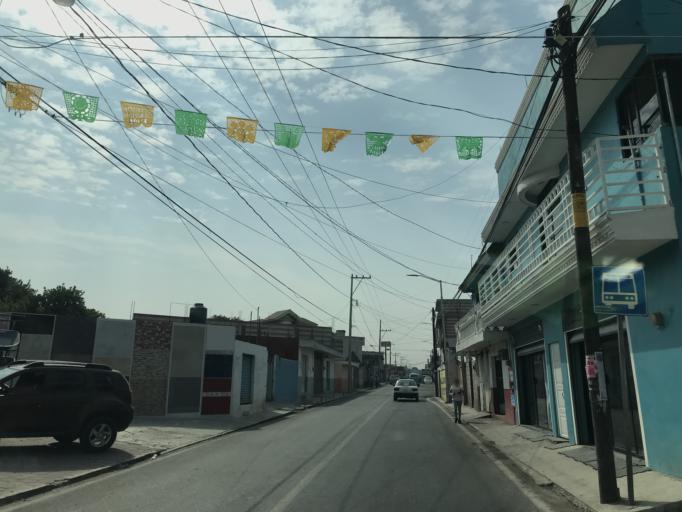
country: MX
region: Tlaxcala
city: Tenancingo
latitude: 19.1458
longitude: -98.1974
